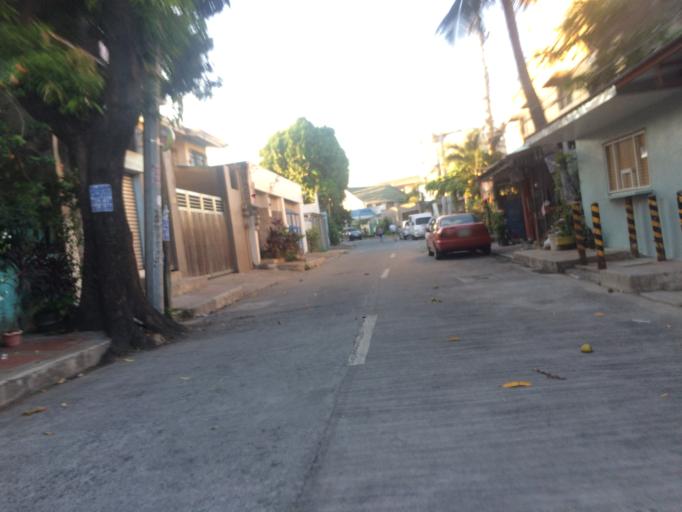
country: PH
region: Calabarzon
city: Bagong Pagasa
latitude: 14.6744
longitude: 121.0180
